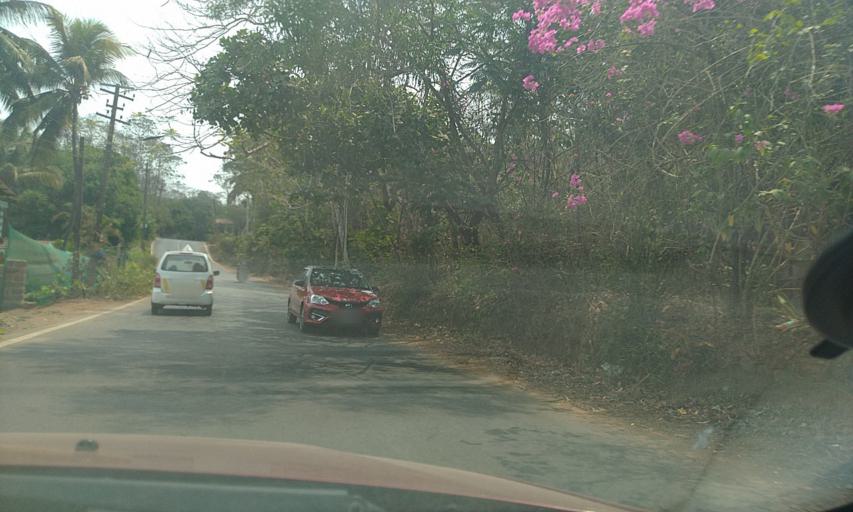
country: IN
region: Goa
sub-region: North Goa
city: Mapuca
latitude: 15.5971
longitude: 73.7902
